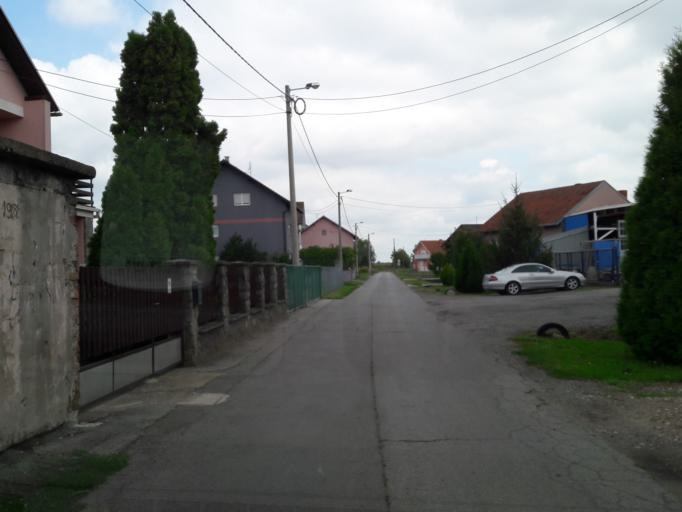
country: HR
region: Osjecko-Baranjska
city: Tenja
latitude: 45.5172
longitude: 18.7308
